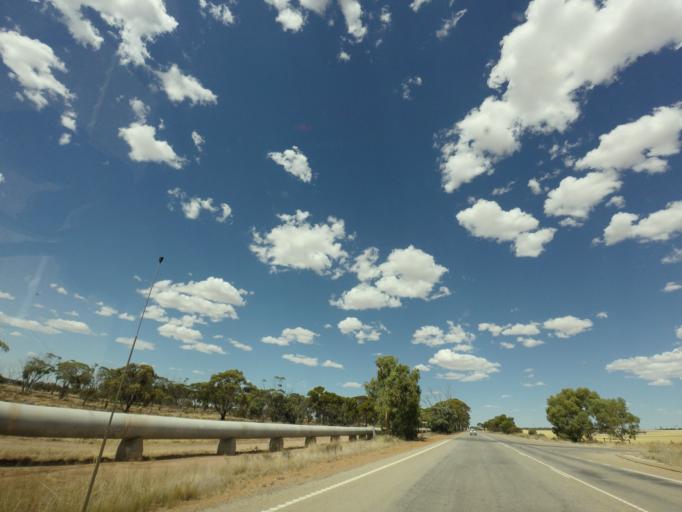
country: AU
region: Western Australia
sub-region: Cunderdin
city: Cunderdin
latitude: -31.6517
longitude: 117.2088
